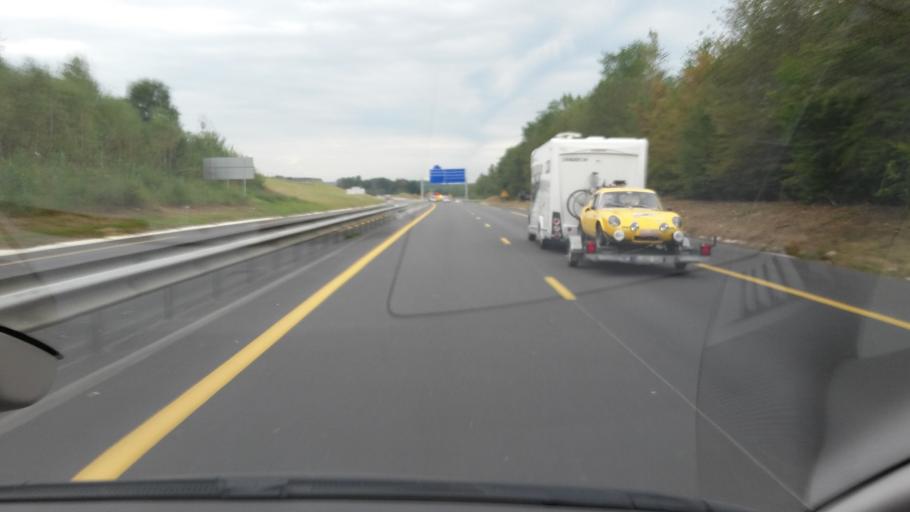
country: FR
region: Champagne-Ardenne
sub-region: Departement des Ardennes
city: La Francheville
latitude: 49.7044
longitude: 4.6974
